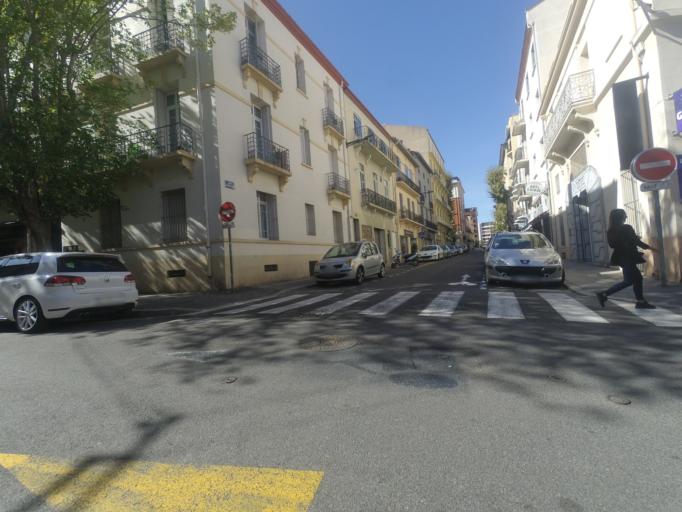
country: FR
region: Languedoc-Roussillon
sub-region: Departement des Pyrenees-Orientales
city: Perpignan
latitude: 42.6998
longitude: 2.8907
